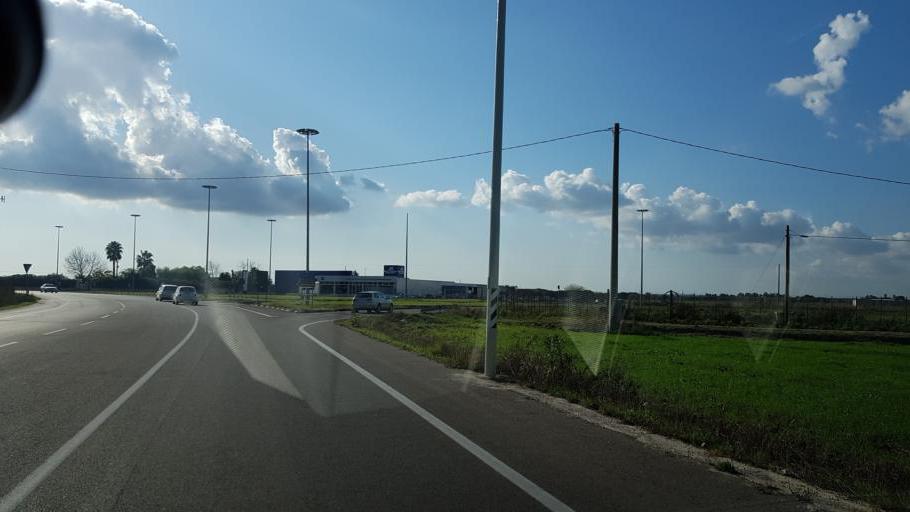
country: IT
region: Apulia
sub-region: Provincia di Lecce
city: Salice Salentino
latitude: 40.3748
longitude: 17.9680
